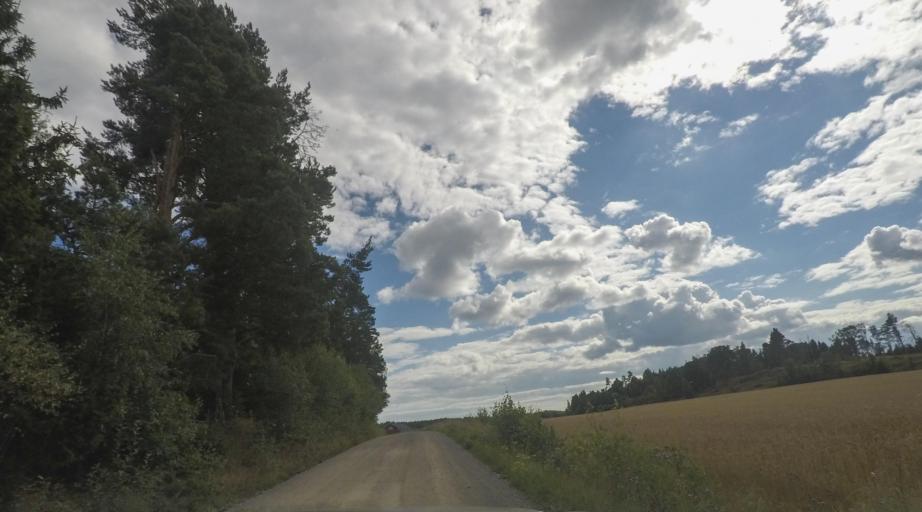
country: SE
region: Stockholm
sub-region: Sodertalje Kommun
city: Pershagen
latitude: 59.1171
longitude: 17.6570
